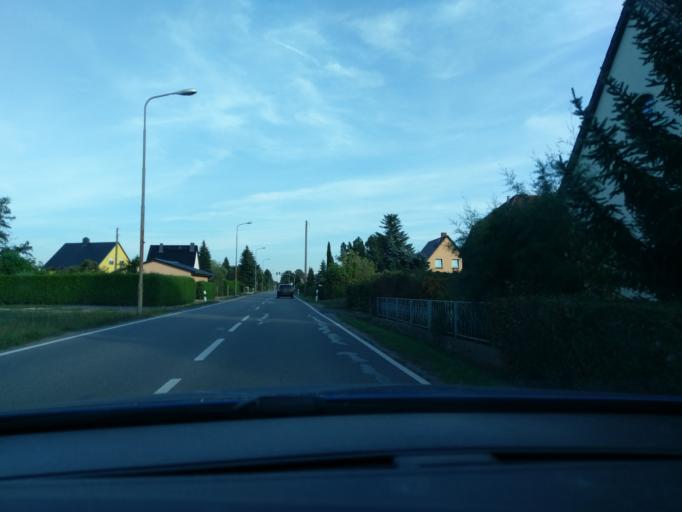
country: DE
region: Saxony
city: Arnsdorf
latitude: 51.0892
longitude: 14.0107
